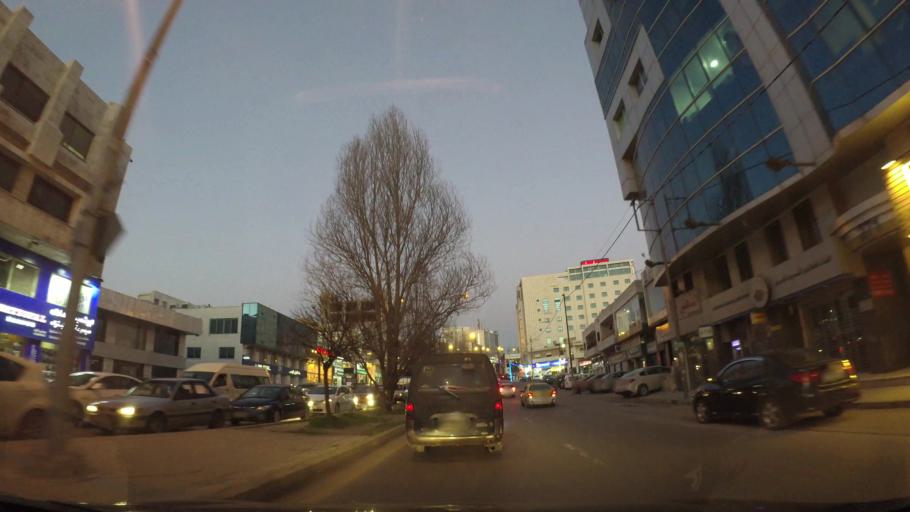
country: JO
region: Amman
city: Al Jubayhah
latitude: 31.9970
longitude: 35.8496
